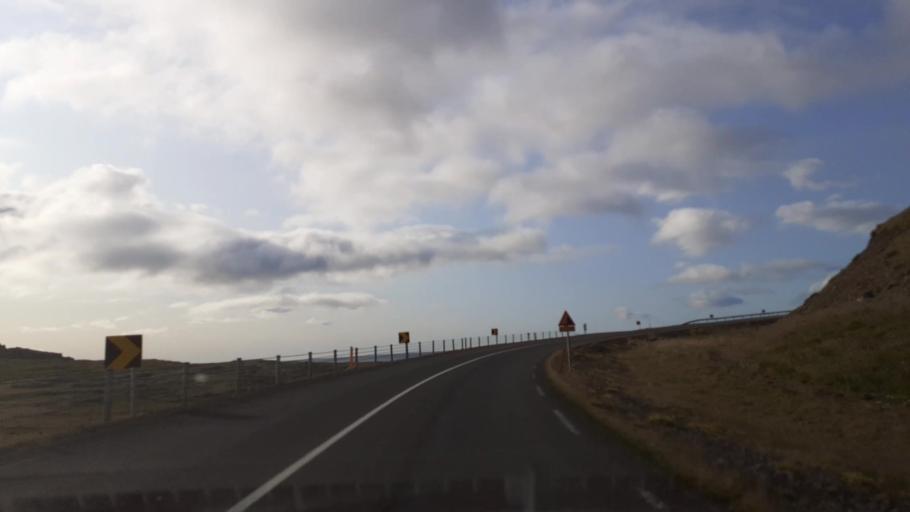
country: IS
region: East
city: Eskifjoerdur
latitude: 64.8074
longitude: -13.8629
